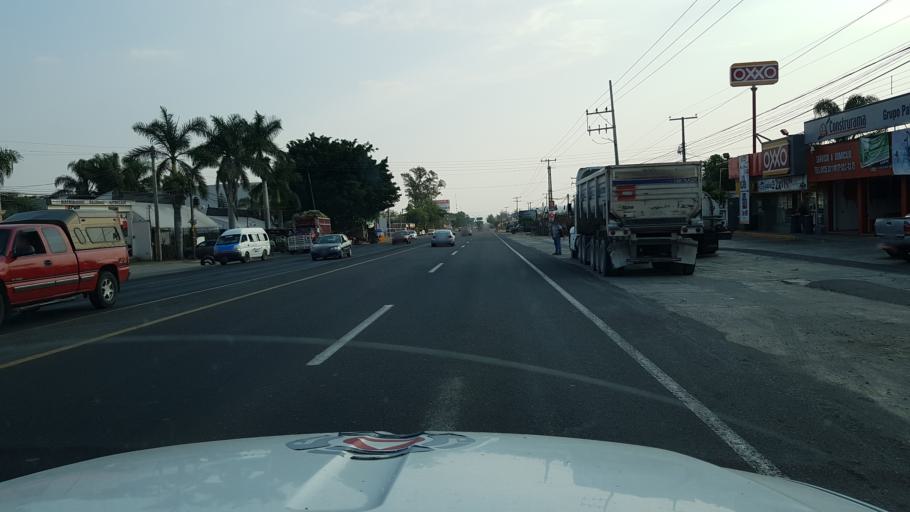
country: MX
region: Morelos
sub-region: Atlatlahucan
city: Colonia San Francisco
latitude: 18.8822
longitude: -98.9189
